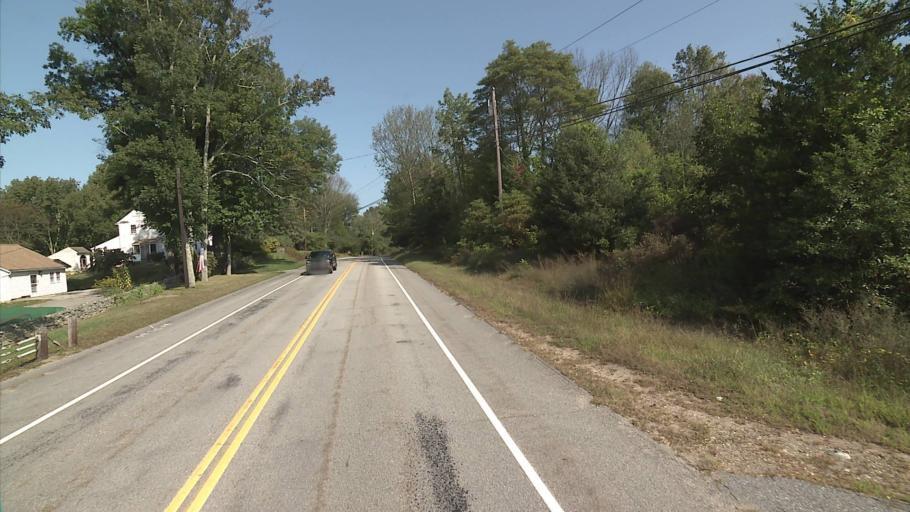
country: US
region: Connecticut
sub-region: Windham County
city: Wauregan
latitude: 41.7320
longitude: -71.9651
